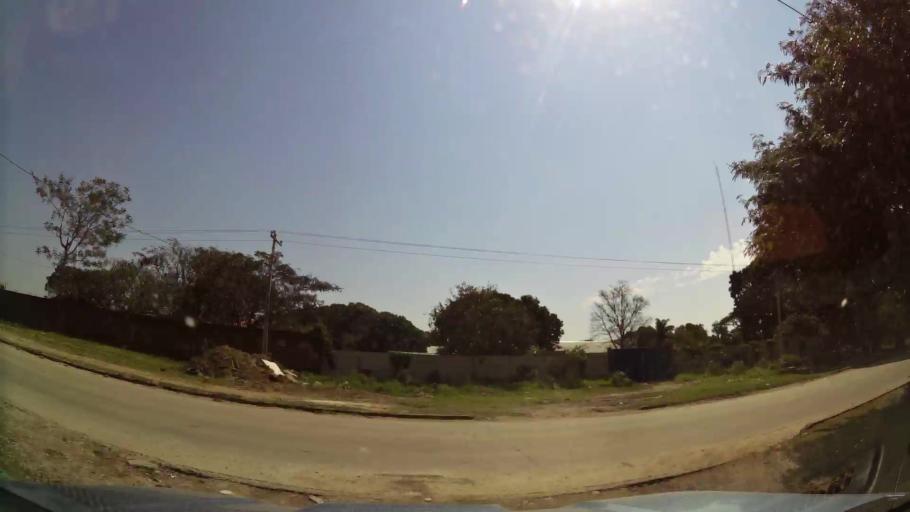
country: BO
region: Santa Cruz
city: Santa Cruz de la Sierra
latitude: -17.7336
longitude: -63.1595
